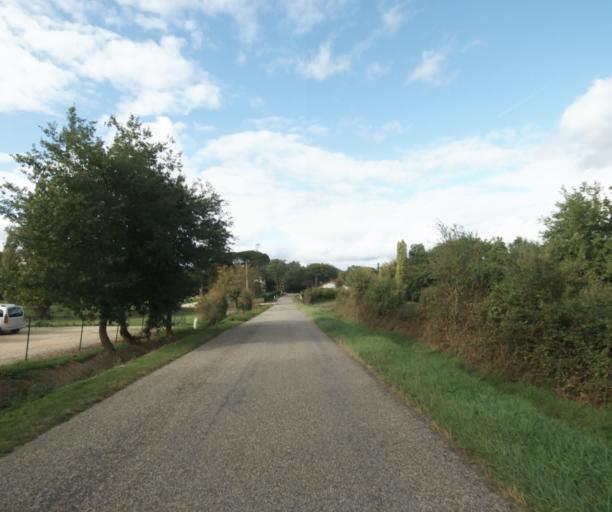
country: FR
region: Midi-Pyrenees
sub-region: Departement du Gers
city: Eauze
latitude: 43.8710
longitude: 0.1008
